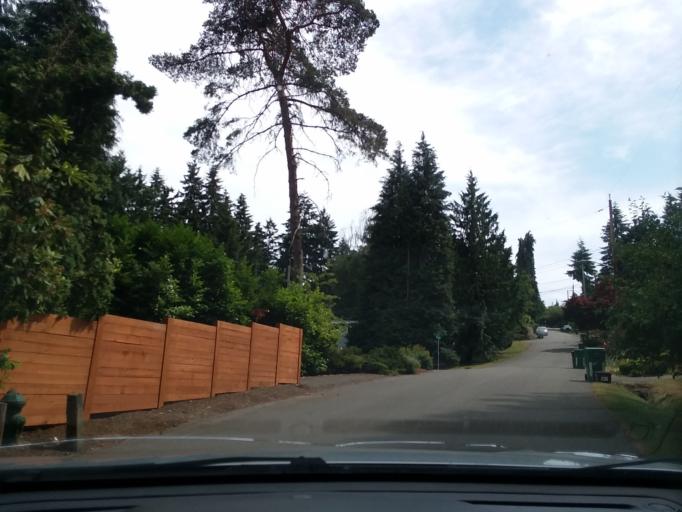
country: US
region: Washington
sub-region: King County
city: Shoreline
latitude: 47.7058
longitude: -122.3150
